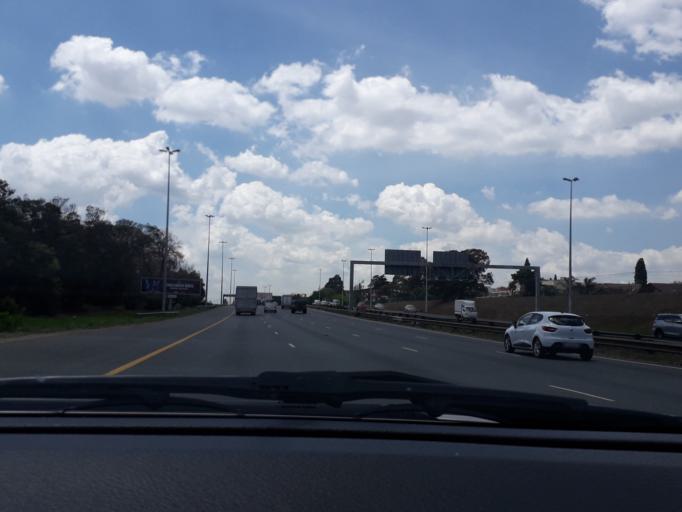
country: ZA
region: Gauteng
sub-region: City of Johannesburg Metropolitan Municipality
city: Johannesburg
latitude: -26.2520
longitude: 27.9951
